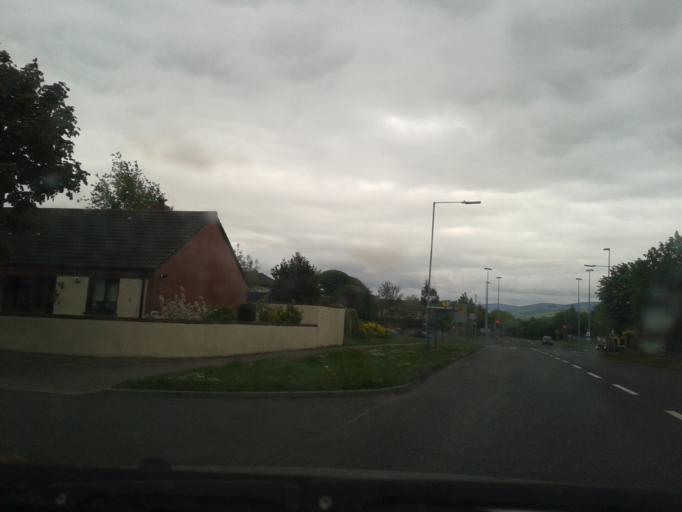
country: IE
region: Leinster
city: Clondalkin
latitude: 53.3216
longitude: -6.4226
